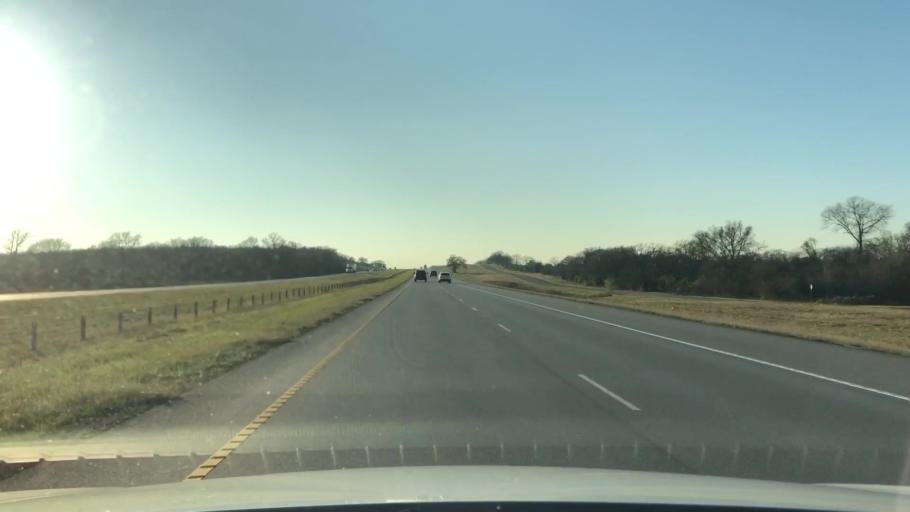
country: US
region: Texas
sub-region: Gonzales County
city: Waelder
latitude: 29.6559
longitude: -97.4395
